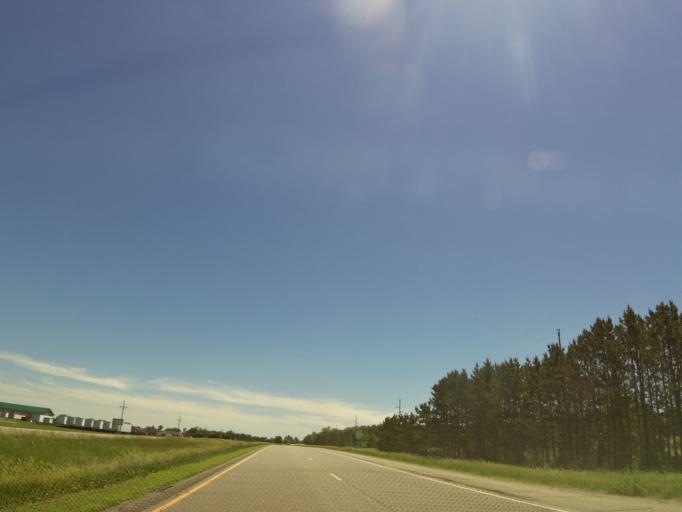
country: US
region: Minnesota
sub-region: Becker County
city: Frazee
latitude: 46.7561
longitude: -95.7694
